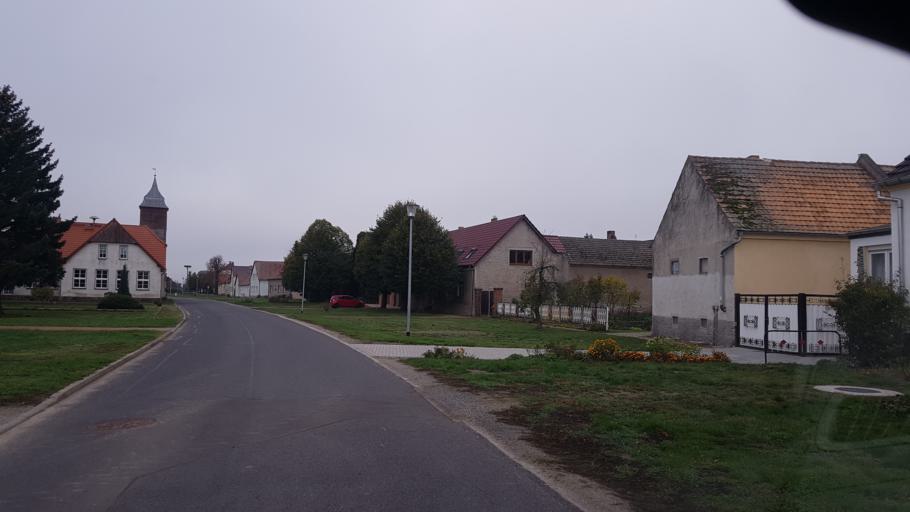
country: DE
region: Brandenburg
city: Schonewalde
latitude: 51.6917
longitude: 13.5388
